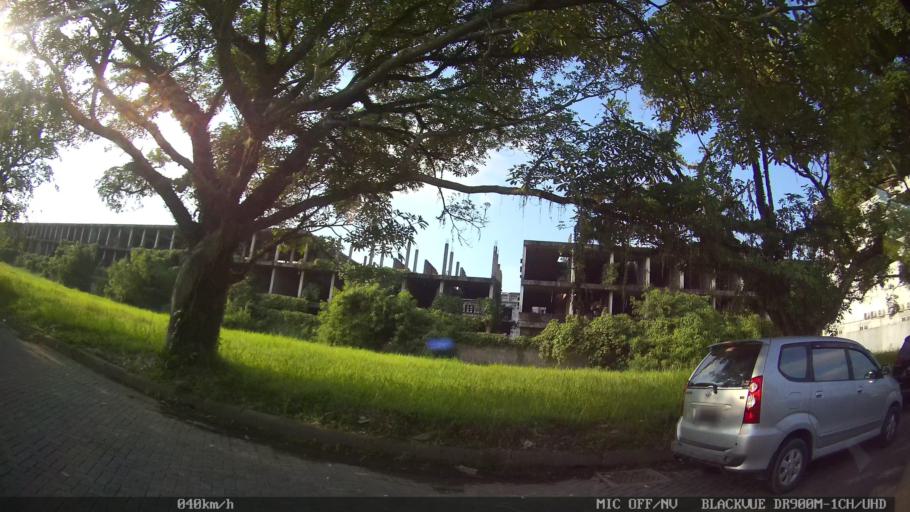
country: ID
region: North Sumatra
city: Medan
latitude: 3.6259
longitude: 98.6462
